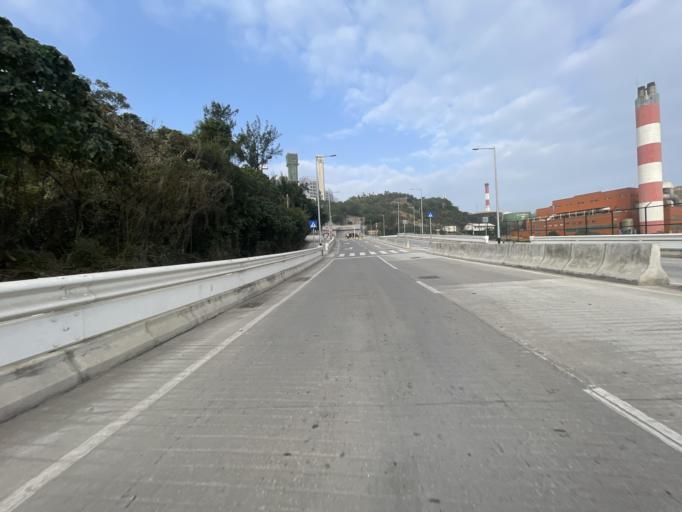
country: MO
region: Macau
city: Macau
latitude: 22.1349
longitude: 113.5810
